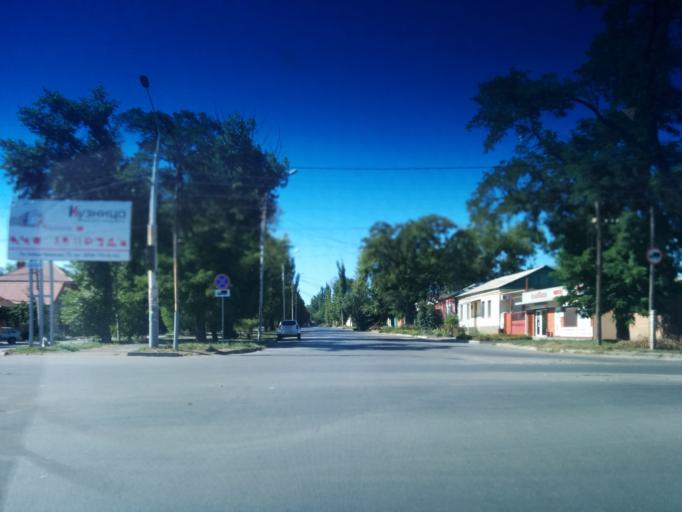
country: RU
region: Rostov
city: Shakhty
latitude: 47.7068
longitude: 40.2245
